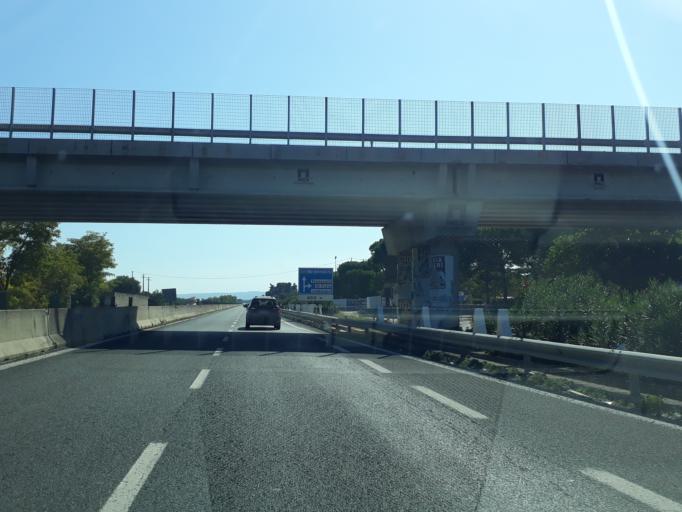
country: IT
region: Apulia
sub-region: Provincia di Bari
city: Monopoli
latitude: 40.9070
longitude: 17.3242
